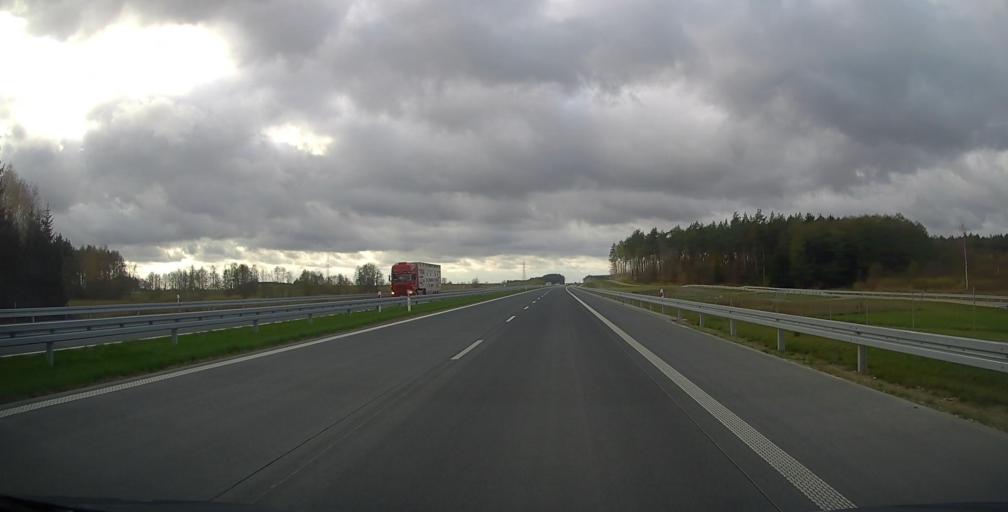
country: PL
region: Podlasie
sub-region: Powiat grajewski
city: Rajgrod
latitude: 53.8686
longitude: 22.6269
